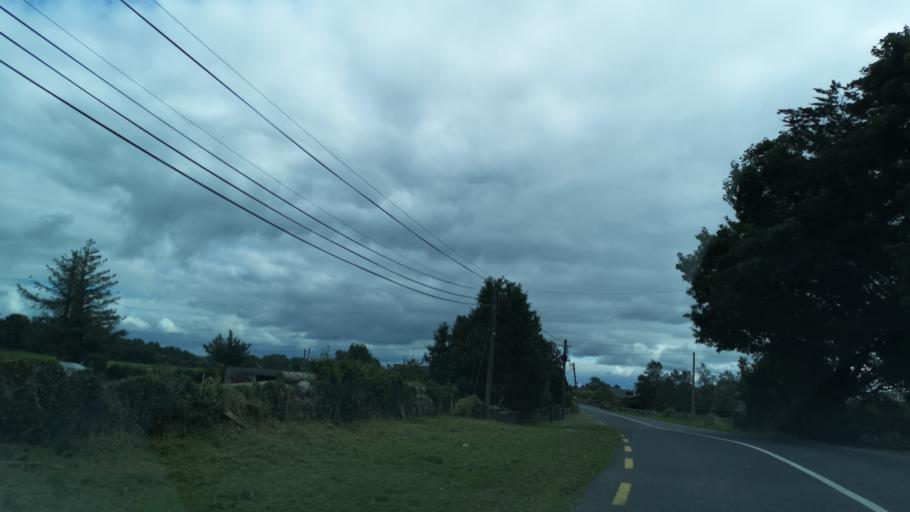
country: IE
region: Connaught
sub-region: County Galway
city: Ballinasloe
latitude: 53.3142
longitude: -8.1672
